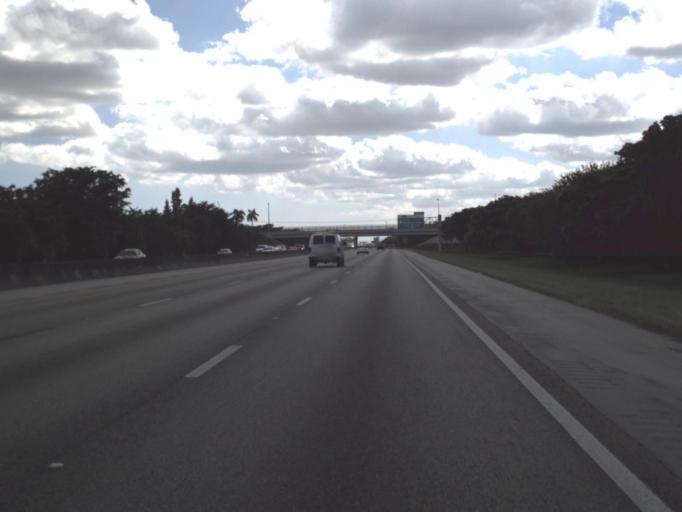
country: US
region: Florida
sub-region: Palm Beach County
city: Boca Pointe
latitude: 26.3213
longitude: -80.1703
